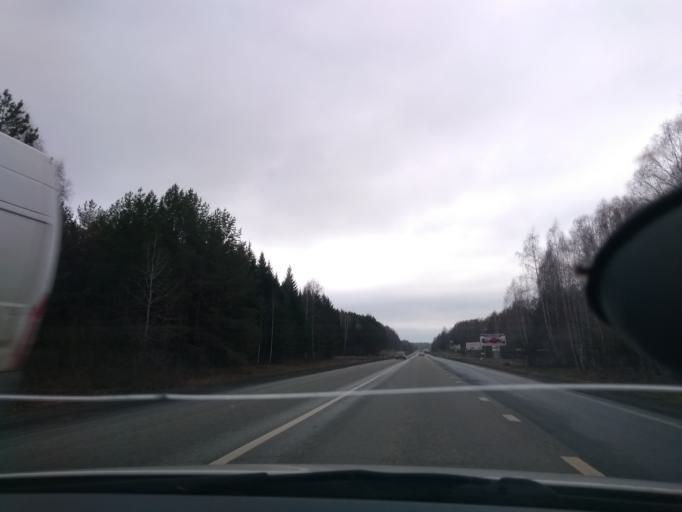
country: RU
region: Perm
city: Kungur
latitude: 57.4128
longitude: 56.8671
